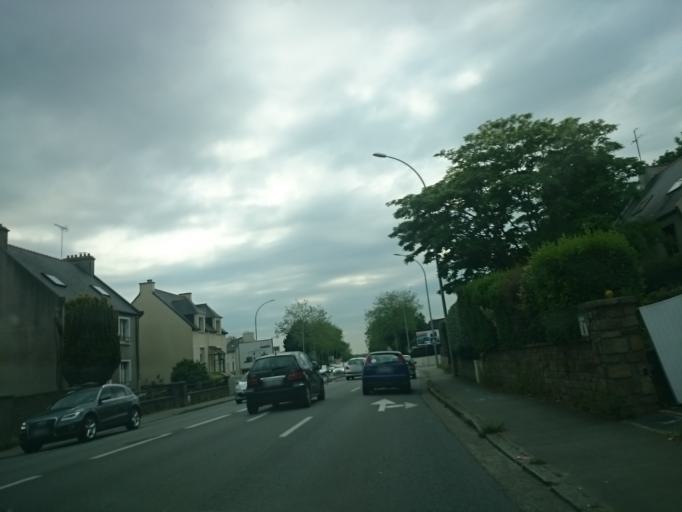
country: FR
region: Brittany
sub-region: Departement du Finistere
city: Brest
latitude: 48.4132
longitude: -4.4967
